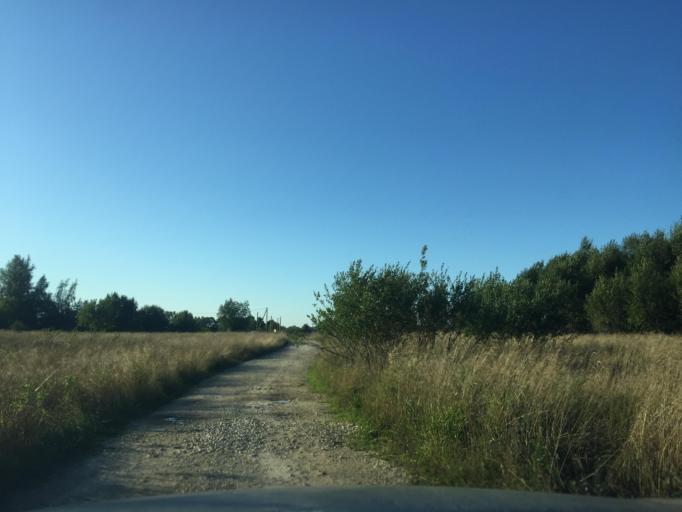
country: RU
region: Leningrad
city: Rozhdestveno
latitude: 59.3299
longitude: 29.9981
